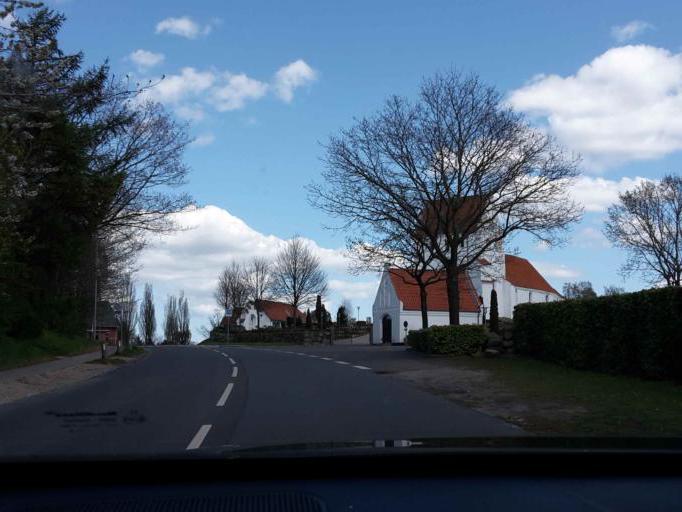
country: DK
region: South Denmark
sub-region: Odense Kommune
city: Bellinge
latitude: 55.4081
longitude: 10.3158
